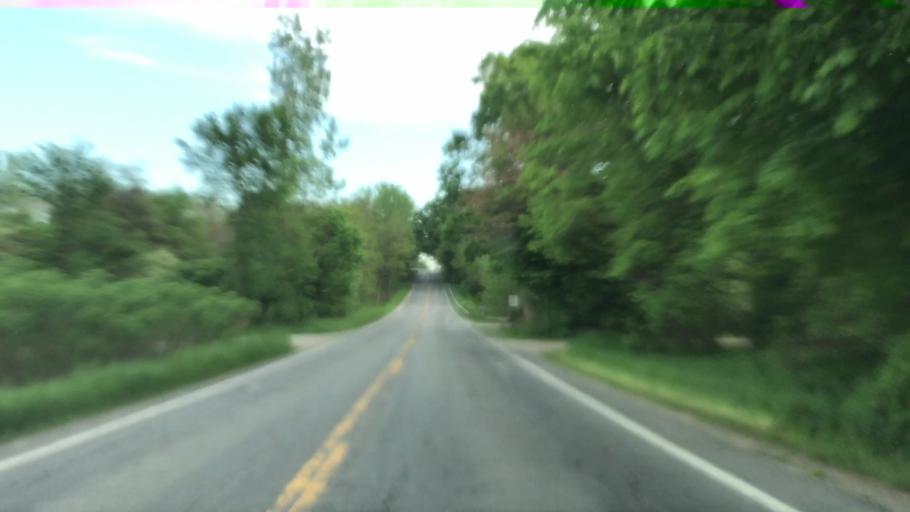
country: US
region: Michigan
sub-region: Lapeer County
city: Almont
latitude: 42.9135
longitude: -83.1433
